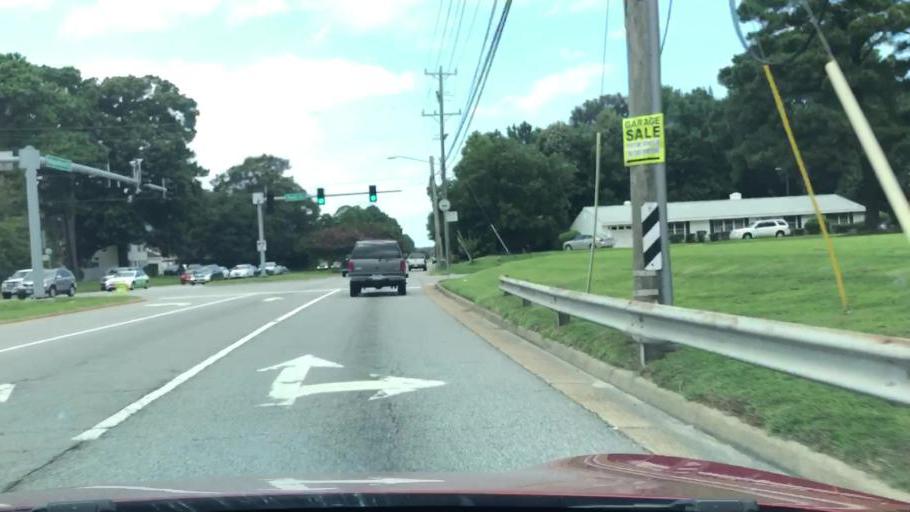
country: US
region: Virginia
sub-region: City of Chesapeake
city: Chesapeake
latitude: 36.8838
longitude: -76.1341
